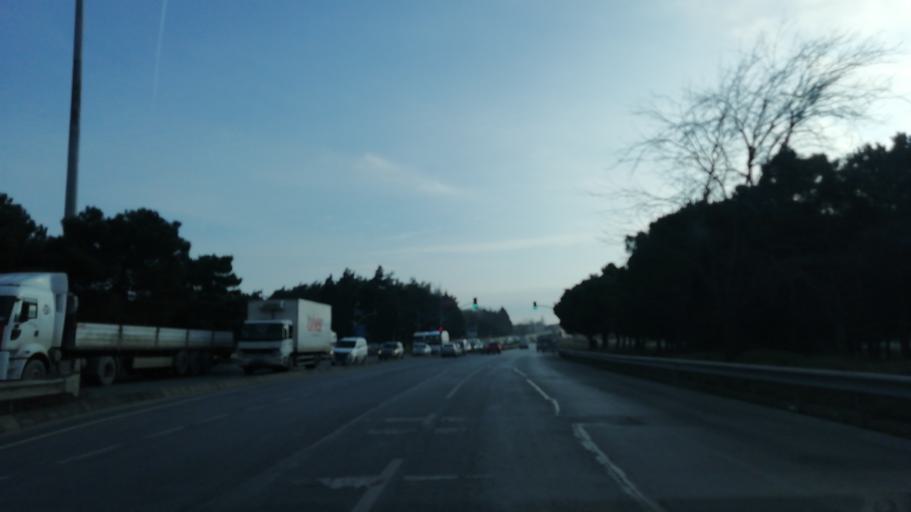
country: TR
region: Istanbul
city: Esenyurt
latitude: 41.1013
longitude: 28.6354
